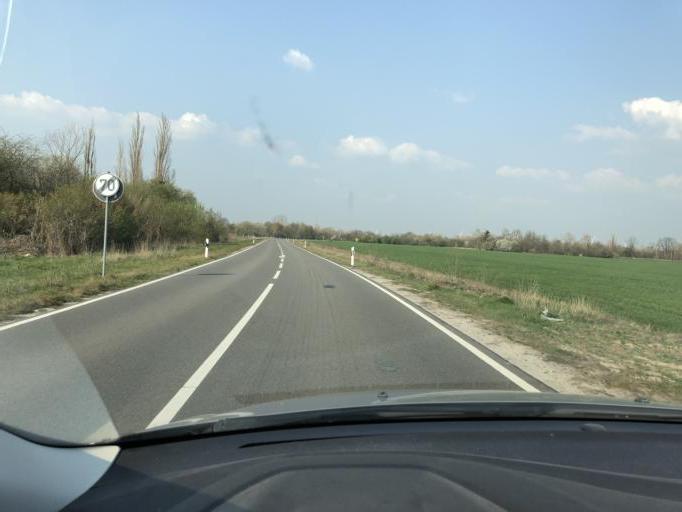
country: DE
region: Saxony
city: Rackwitz
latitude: 51.4301
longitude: 12.3514
